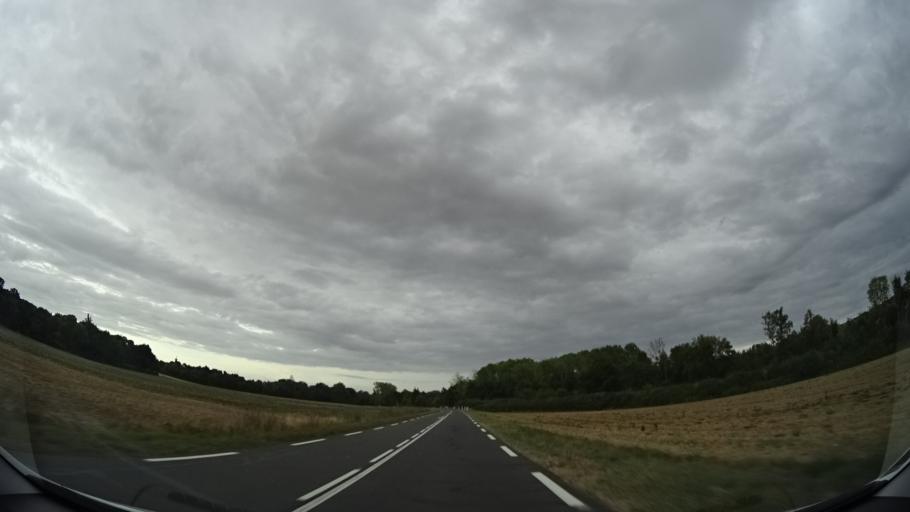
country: FR
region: Centre
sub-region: Departement du Loiret
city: Trigueres
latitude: 47.9361
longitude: 2.9562
